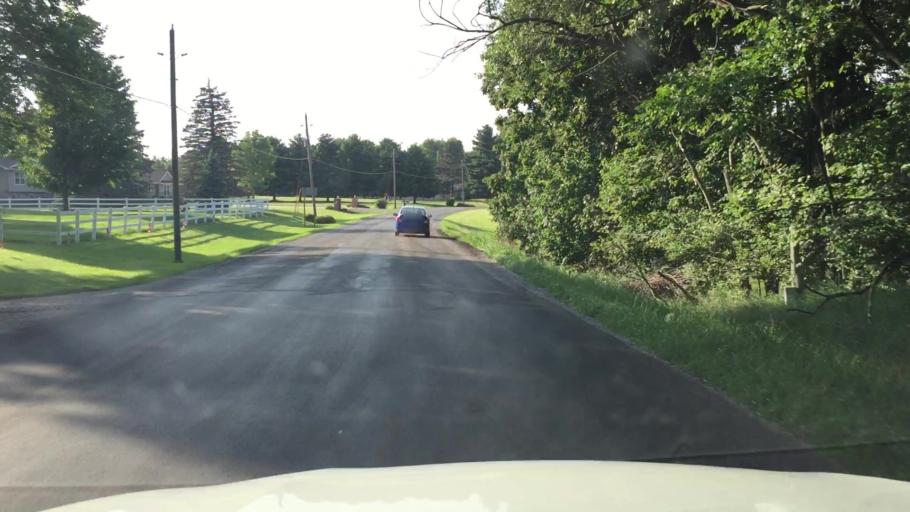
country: US
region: Iowa
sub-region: Linn County
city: Ely
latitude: 41.8218
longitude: -91.6238
